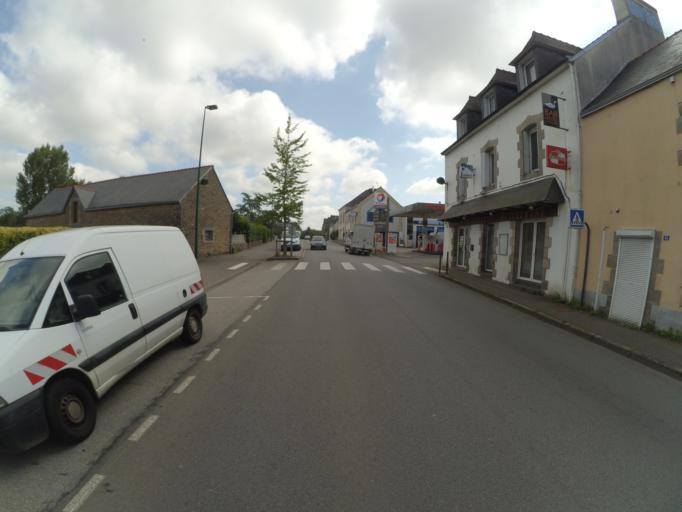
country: FR
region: Brittany
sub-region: Departement du Finistere
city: Rosporden
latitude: 47.9579
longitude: -3.8236
